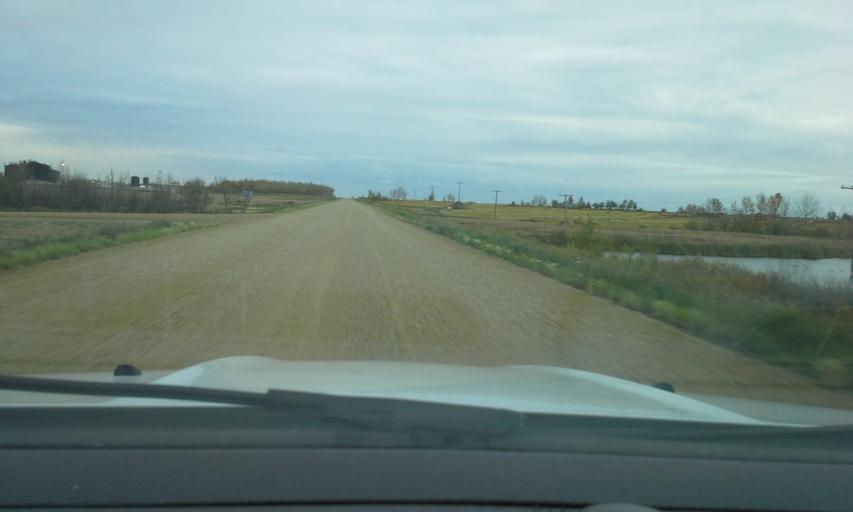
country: CA
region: Saskatchewan
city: Lloydminster
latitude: 53.2799
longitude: -109.8084
